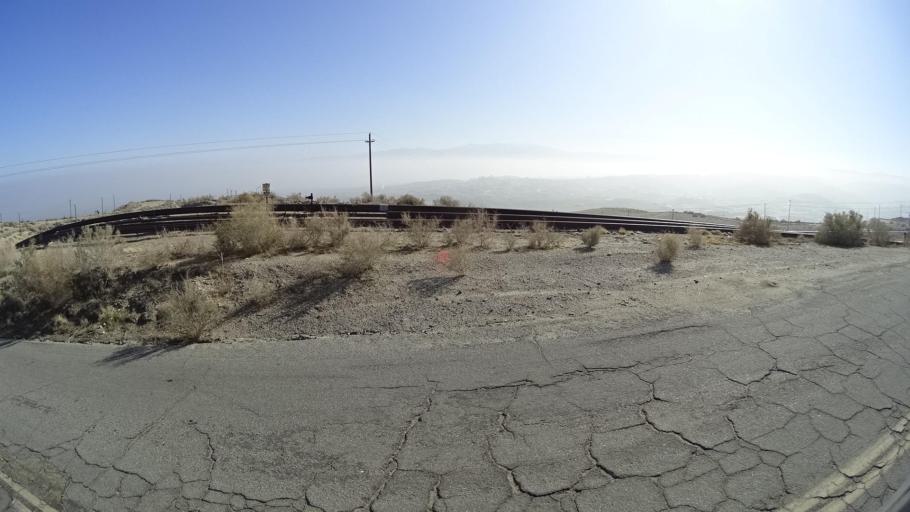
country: US
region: California
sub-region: Kern County
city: South Taft
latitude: 35.1152
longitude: -119.4598
